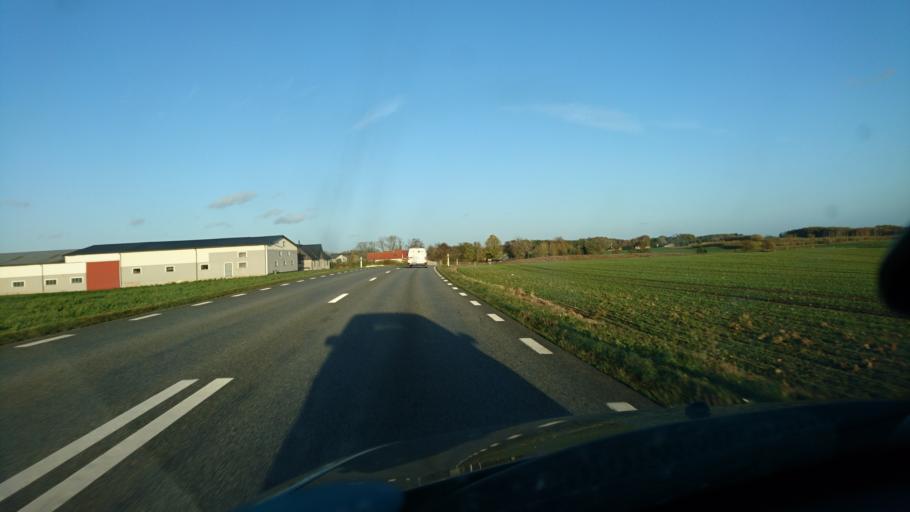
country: SE
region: Skane
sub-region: Tomelilla Kommun
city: Tomelilla
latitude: 55.5504
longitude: 14.0661
